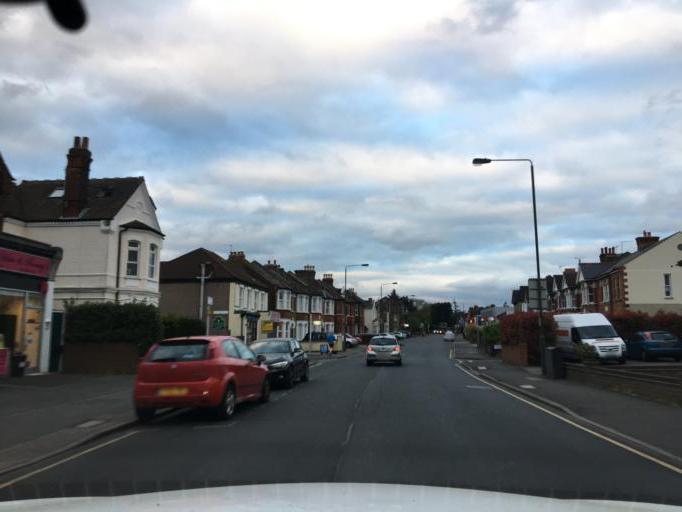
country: GB
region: England
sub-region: Greater London
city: Sidcup
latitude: 51.4301
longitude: 0.0866
